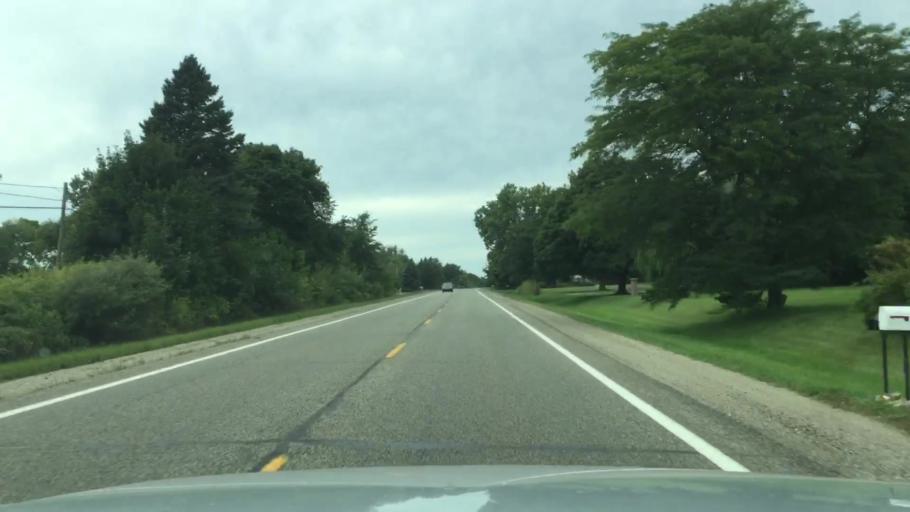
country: US
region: Michigan
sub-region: Shiawassee County
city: Durand
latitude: 42.9339
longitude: -84.0115
